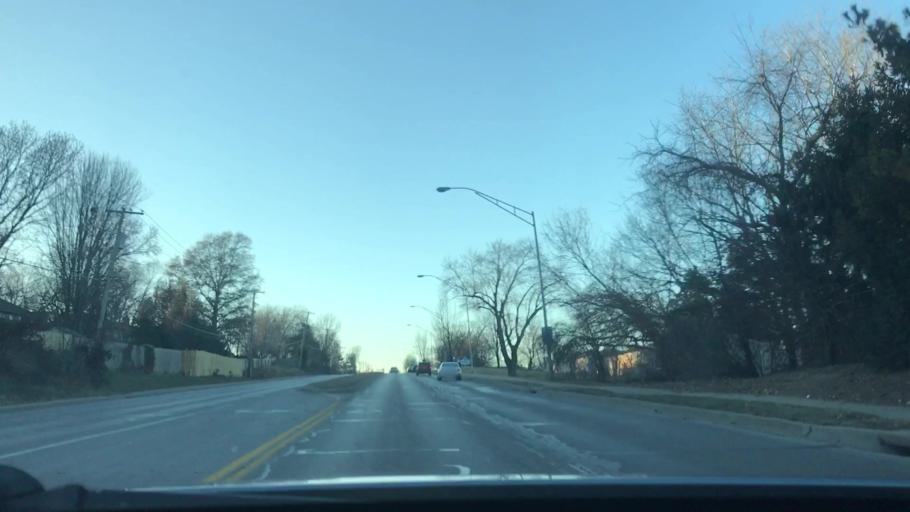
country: US
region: Missouri
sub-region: Platte County
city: Weatherby Lake
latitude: 39.2467
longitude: -94.6381
